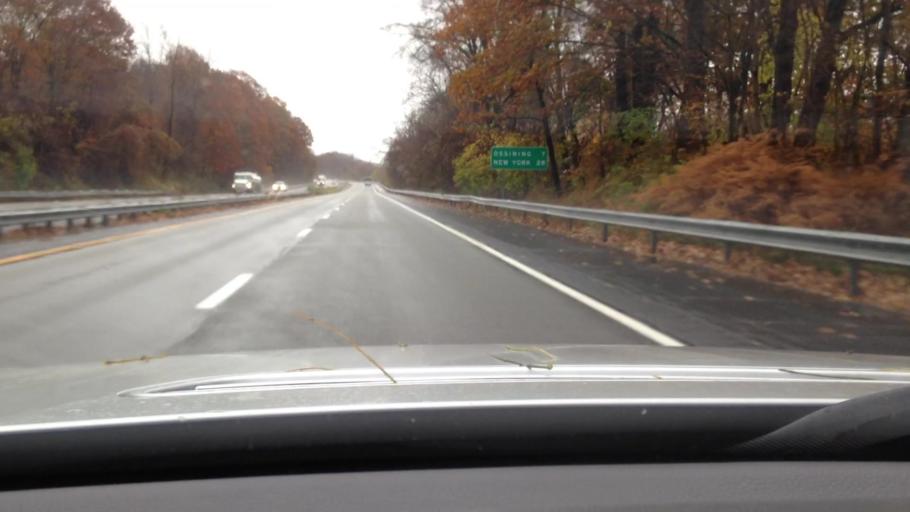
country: US
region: New York
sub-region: Westchester County
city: Montrose
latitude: 41.2587
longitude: -73.9303
